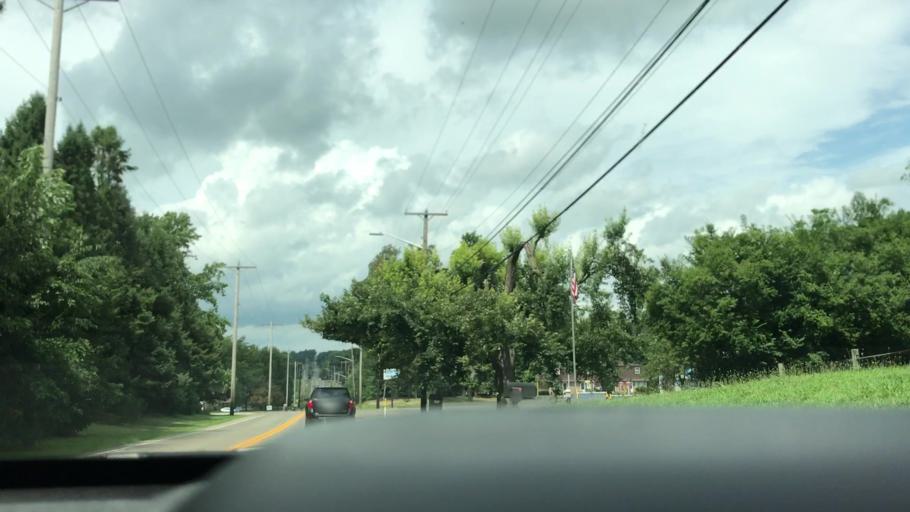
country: US
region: Ohio
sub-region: Stark County
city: Brewster
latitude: 40.7223
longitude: -81.5970
